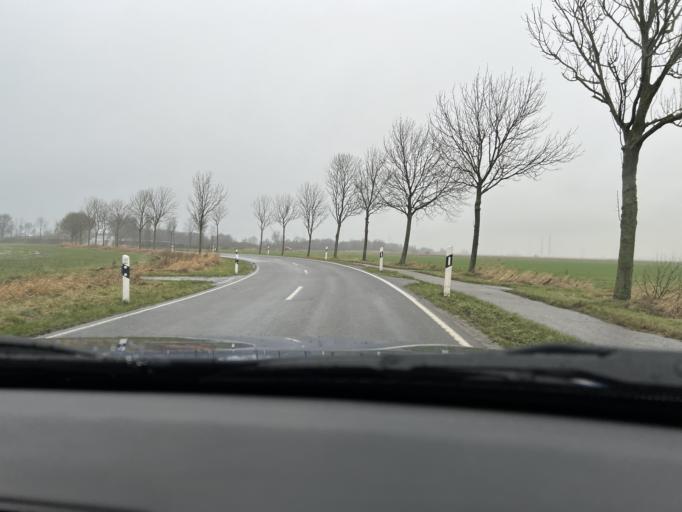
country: DE
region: Schleswig-Holstein
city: Stelle-Wittenwurth
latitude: 54.2406
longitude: 9.0438
